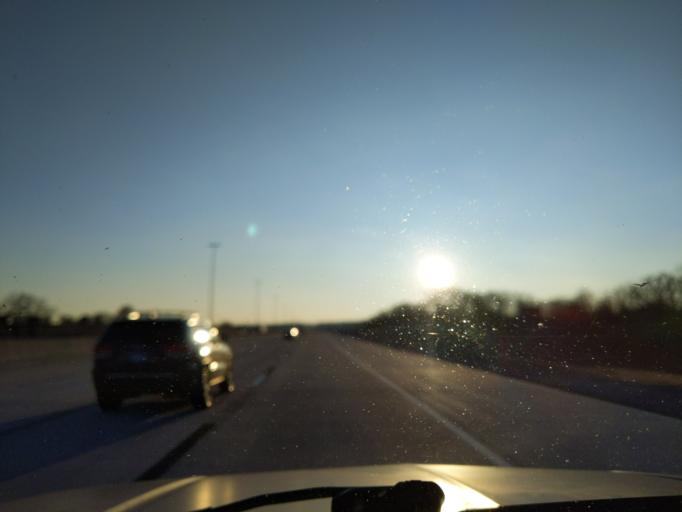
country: US
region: Oklahoma
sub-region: Creek County
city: Kellyville
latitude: 35.9294
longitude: -96.2742
